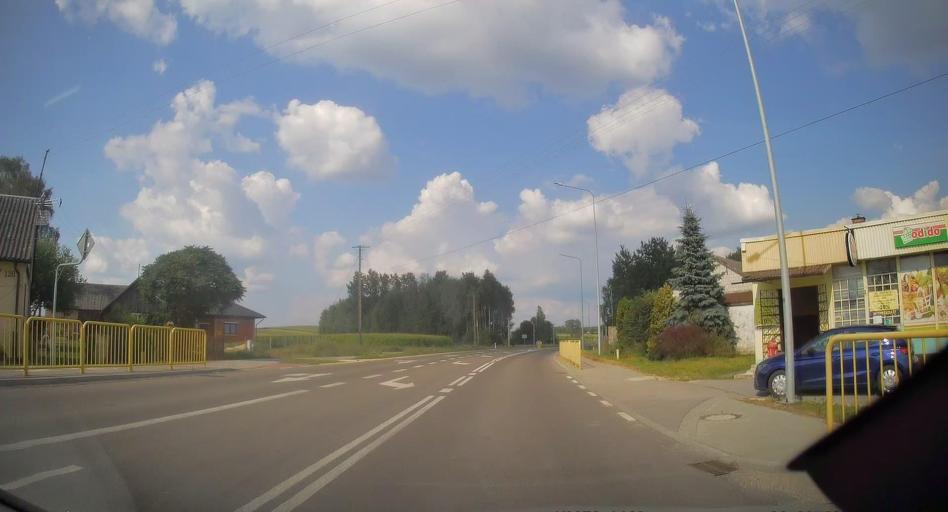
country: PL
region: Swietokrzyskie
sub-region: Powiat kielecki
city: Lopuszno
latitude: 50.9873
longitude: 20.2571
